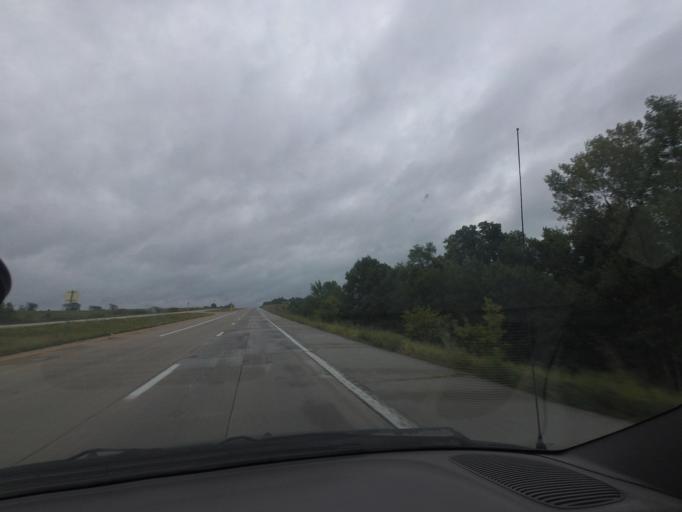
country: US
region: Missouri
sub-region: Marion County
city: Monroe City
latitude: 39.6736
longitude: -91.8855
